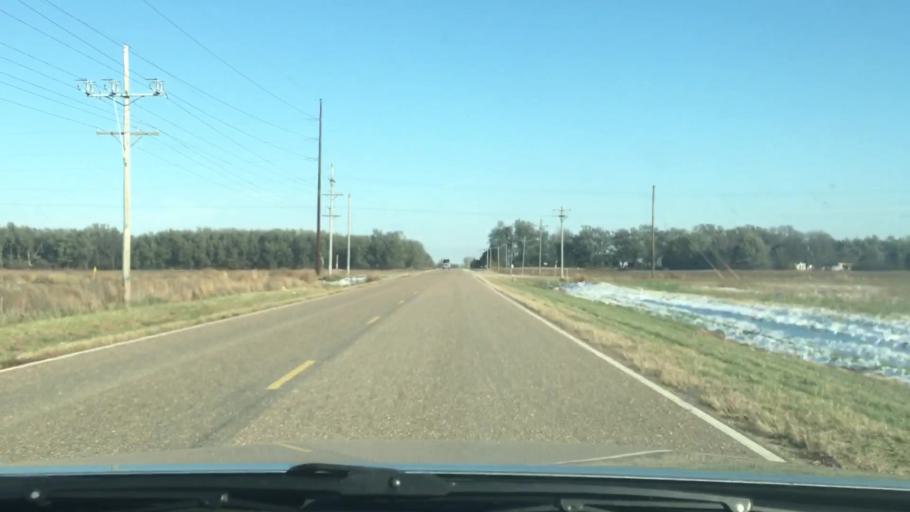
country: US
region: Kansas
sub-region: Rice County
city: Lyons
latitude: 38.2895
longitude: -98.1848
